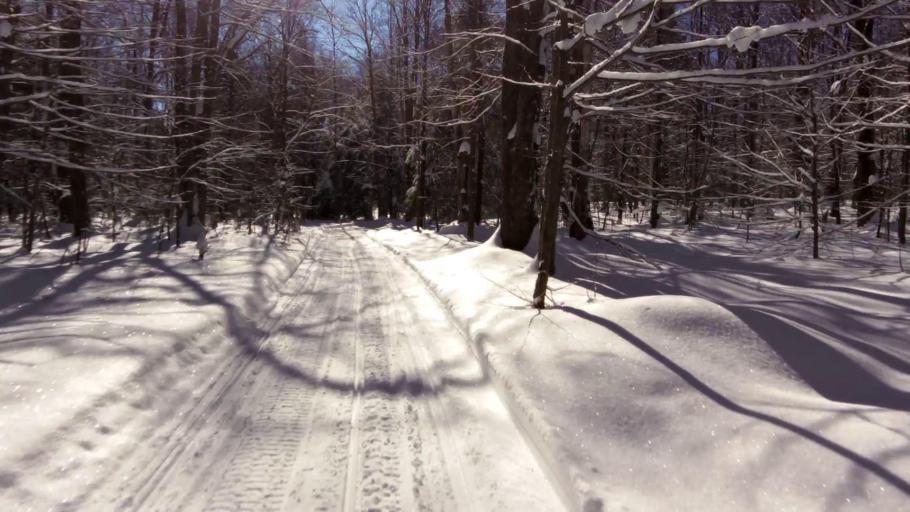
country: US
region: New York
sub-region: Chautauqua County
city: Fredonia
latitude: 42.3490
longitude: -79.1870
